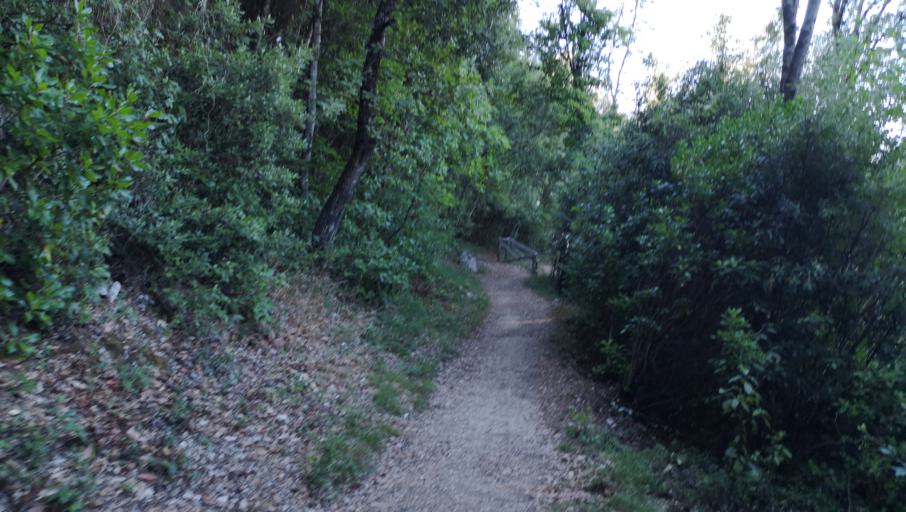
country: IT
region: Umbria
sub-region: Provincia di Terni
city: Narni
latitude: 42.5081
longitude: 12.5366
